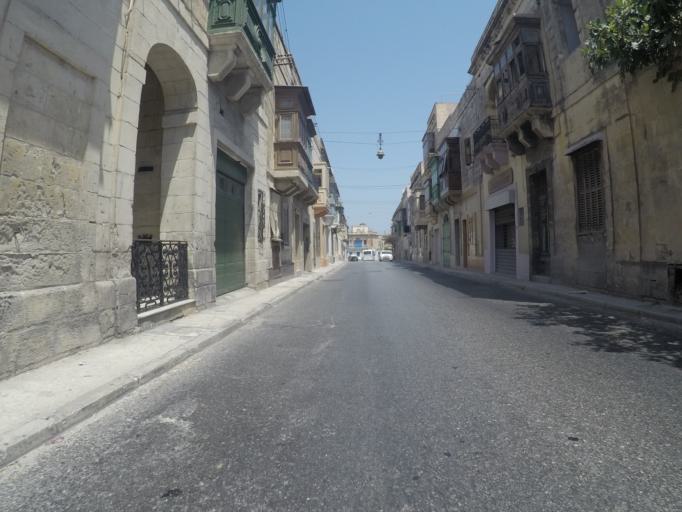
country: MT
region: Ir-Rabat
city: Rabat
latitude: 35.8796
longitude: 14.4008
